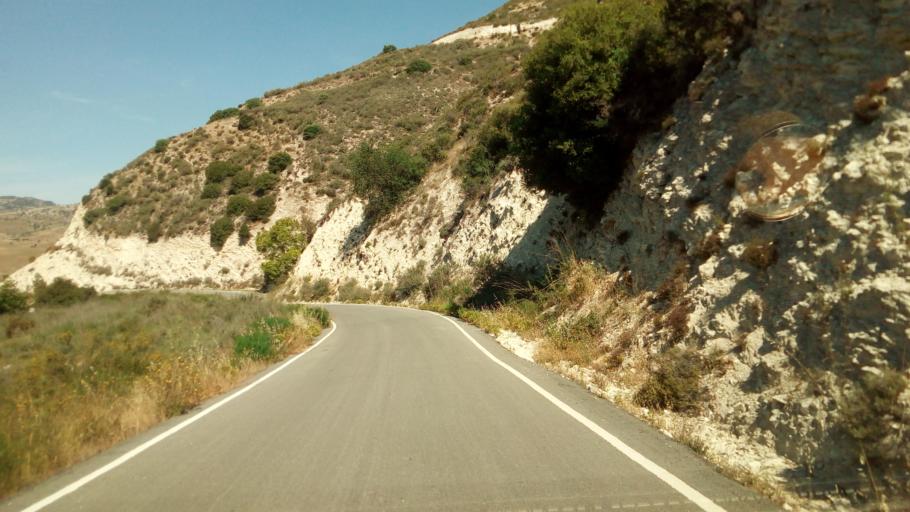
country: CY
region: Limassol
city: Pachna
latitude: 34.8151
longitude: 32.7262
